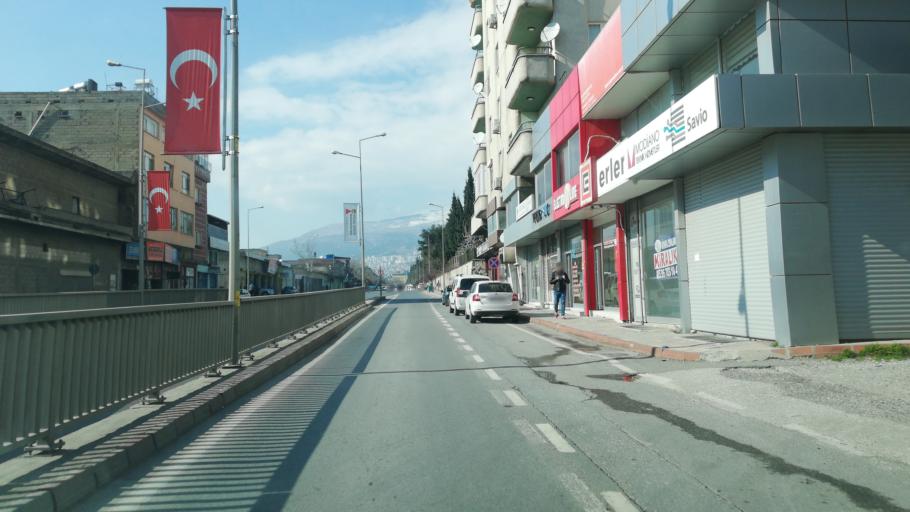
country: TR
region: Kahramanmaras
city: Kahramanmaras
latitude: 37.5721
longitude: 36.9411
